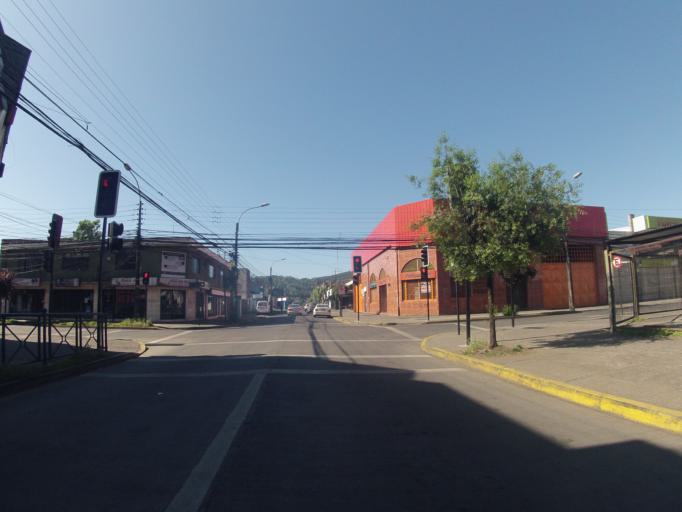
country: CL
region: Araucania
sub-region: Provincia de Cautin
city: Temuco
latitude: -38.7392
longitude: -72.5934
